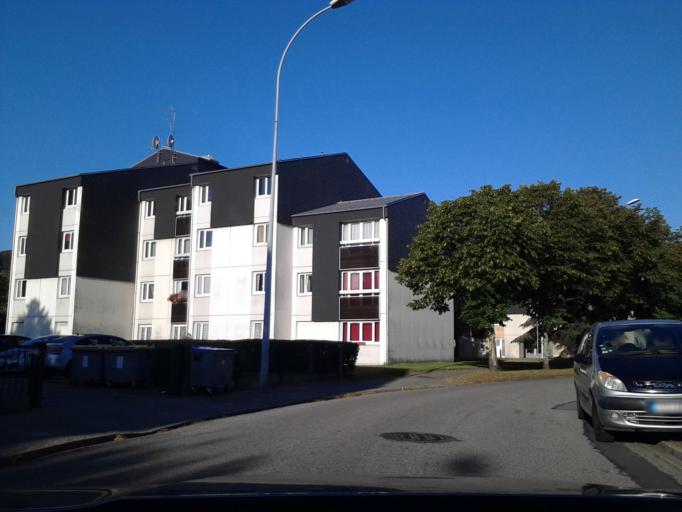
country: FR
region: Lower Normandy
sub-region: Departement de la Manche
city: Cherbourg-Octeville
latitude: 49.6361
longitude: -1.6050
